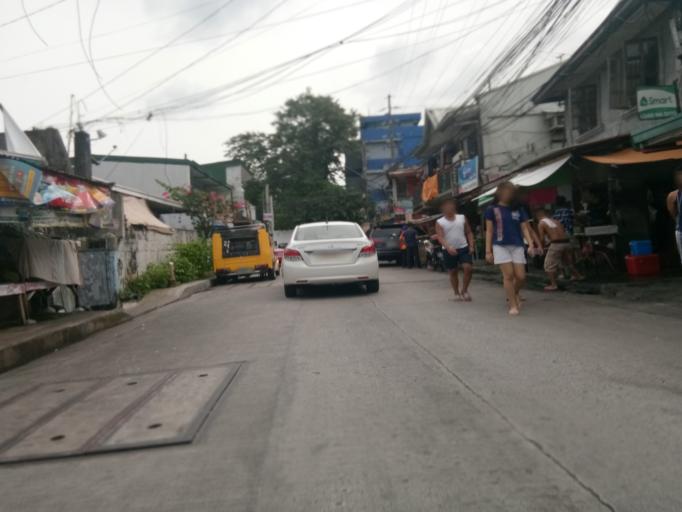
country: PH
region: Metro Manila
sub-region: San Juan
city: San Juan
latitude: 14.6108
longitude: 121.0520
